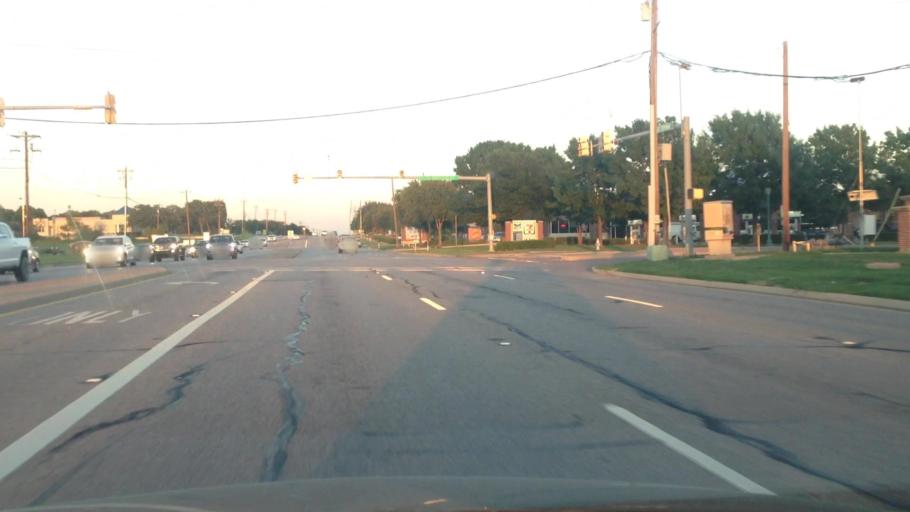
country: US
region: Texas
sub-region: Tarrant County
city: Keller
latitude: 32.9344
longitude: -97.2191
